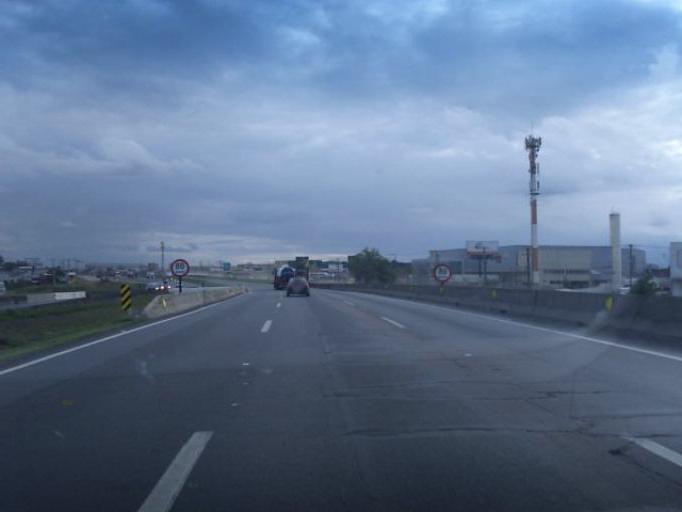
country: BR
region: Parana
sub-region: Sao Jose Dos Pinhais
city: Sao Jose dos Pinhais
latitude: -25.5364
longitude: -49.1488
